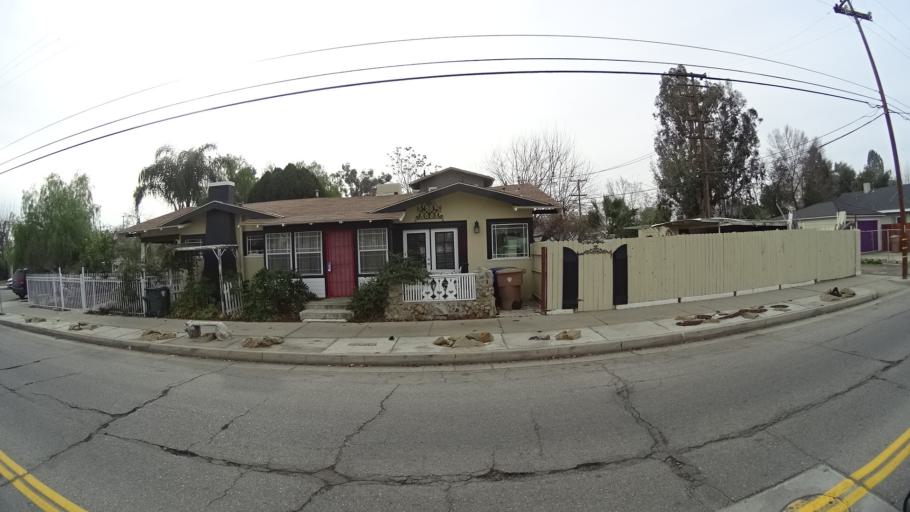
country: US
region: California
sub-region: Kern County
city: Bakersfield
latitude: 35.3614
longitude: -119.0247
